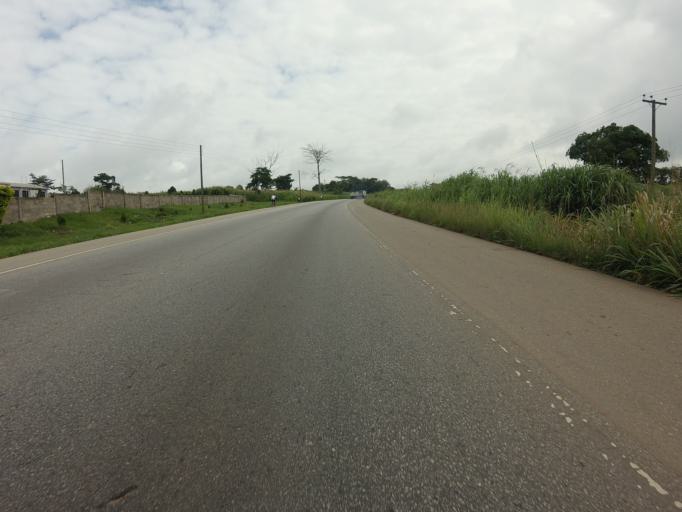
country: GH
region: Ashanti
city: Tafo
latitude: 6.9736
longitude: -1.6853
